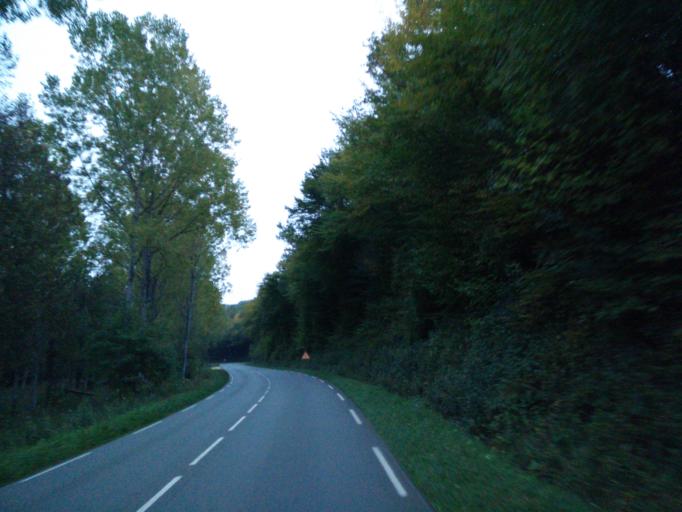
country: FR
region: Aquitaine
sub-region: Departement de la Dordogne
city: Sarlat-la-Caneda
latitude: 44.9123
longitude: 1.1485
